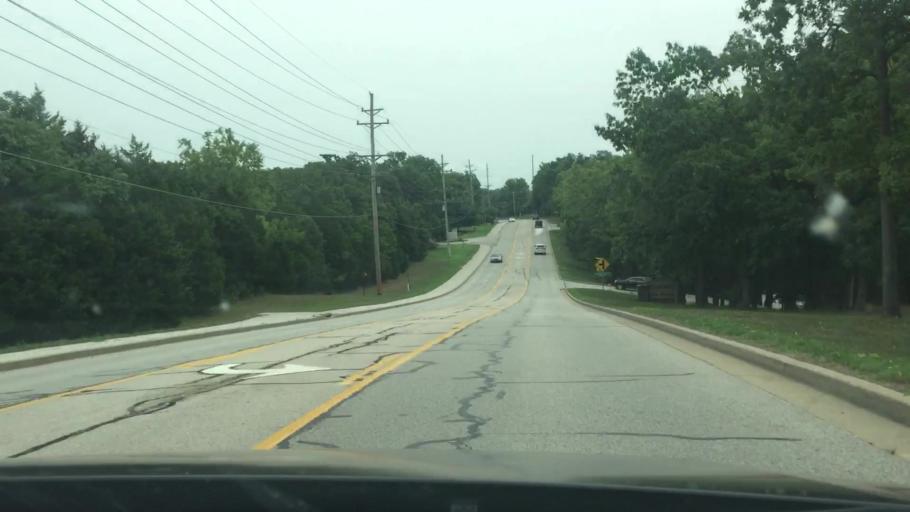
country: US
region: Missouri
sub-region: Camden County
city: Four Seasons
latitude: 38.1911
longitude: -92.7000
